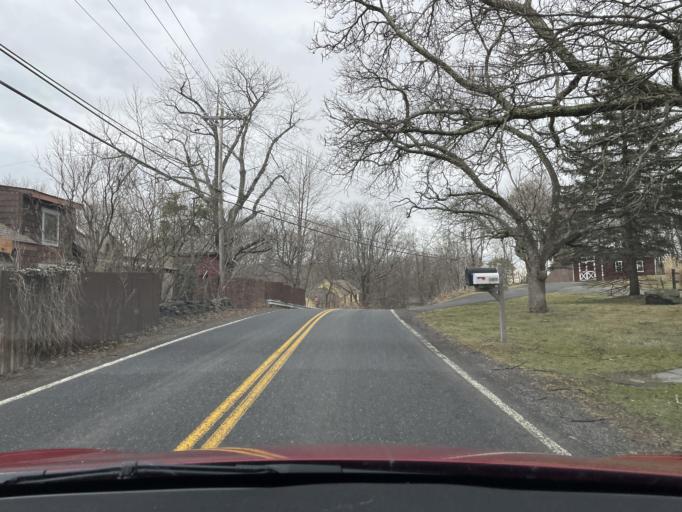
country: US
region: New York
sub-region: Ulster County
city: Manorville
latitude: 42.1121
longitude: -74.0466
